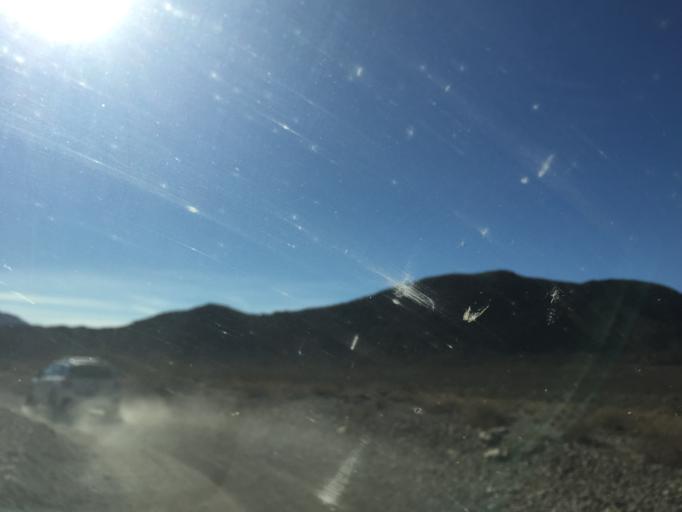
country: US
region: California
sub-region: Inyo County
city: Lone Pine
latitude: 36.7932
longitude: -117.5198
